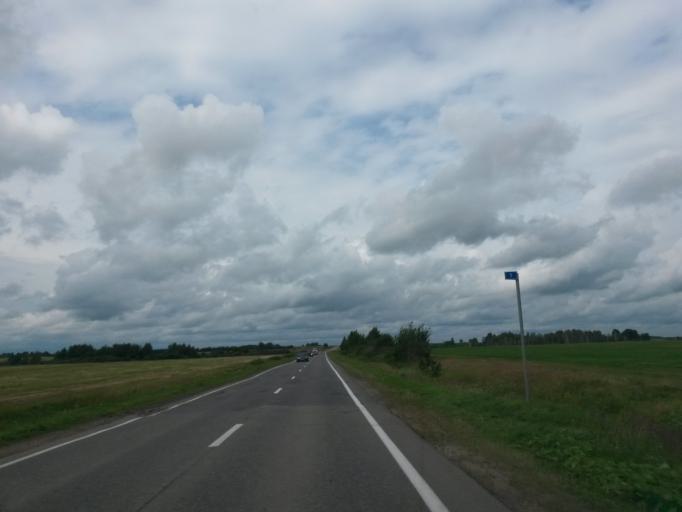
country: RU
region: Jaroslavl
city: Yaroslavl
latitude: 57.7439
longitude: 39.8864
